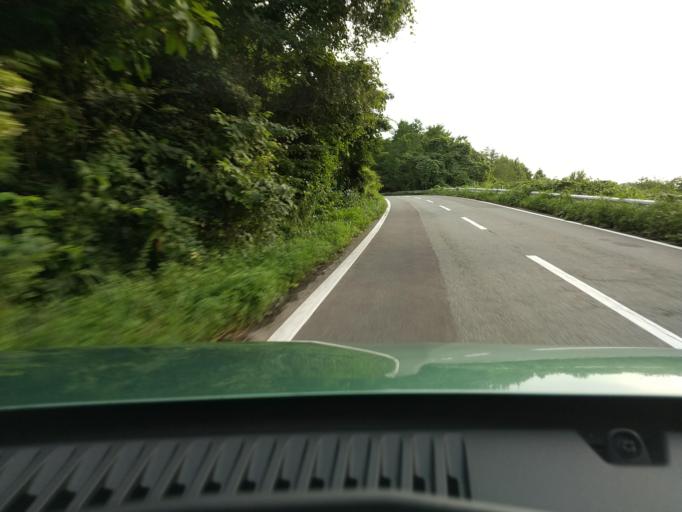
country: JP
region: Akita
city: Akita
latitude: 39.7563
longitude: 140.1596
